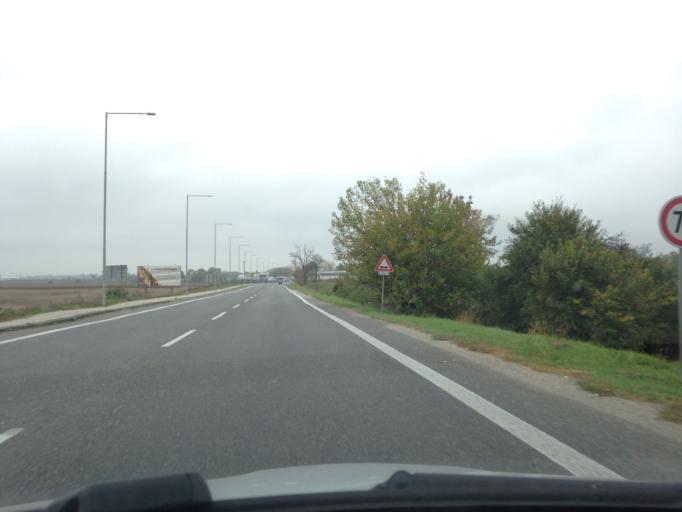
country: SK
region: Nitriansky
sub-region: Okres Nove Zamky
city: Sturovo
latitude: 47.7986
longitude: 18.6917
